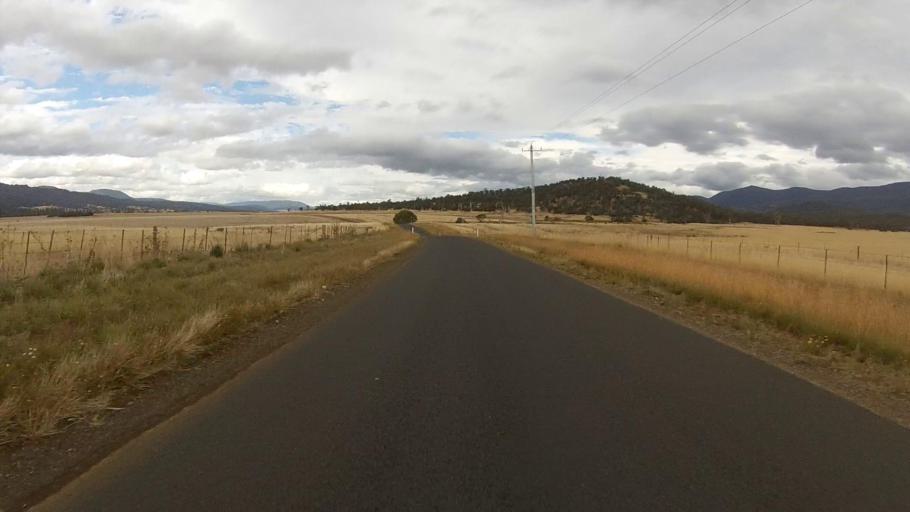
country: AU
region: Tasmania
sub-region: Northern Midlands
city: Evandale
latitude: -41.8275
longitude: 147.7827
